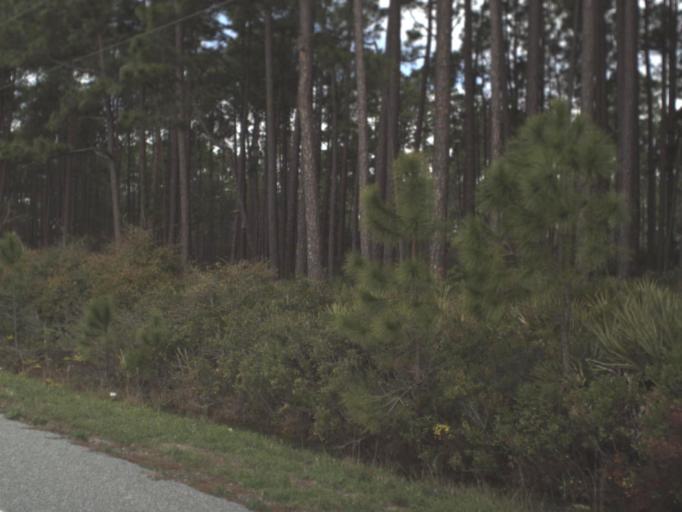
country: US
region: Florida
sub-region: Franklin County
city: Eastpoint
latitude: 29.7686
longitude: -84.8017
